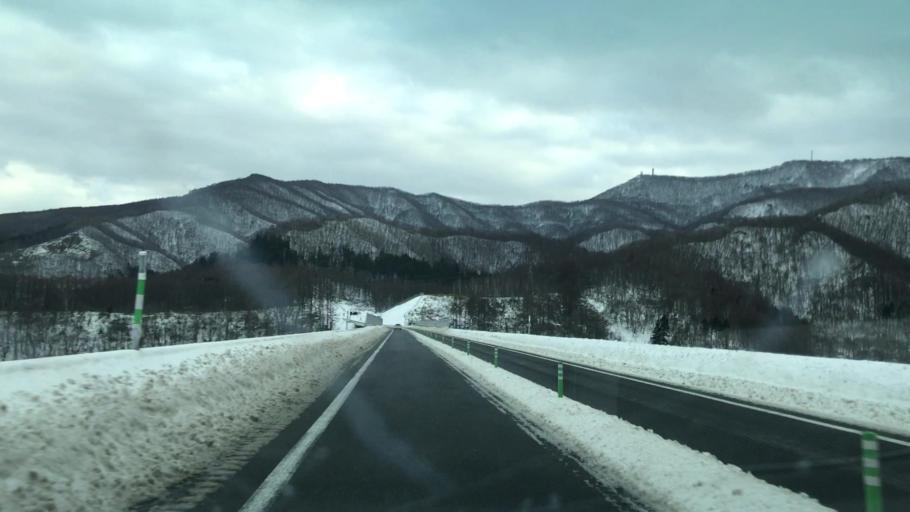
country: JP
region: Hokkaido
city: Otaru
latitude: 43.1661
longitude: 140.9862
